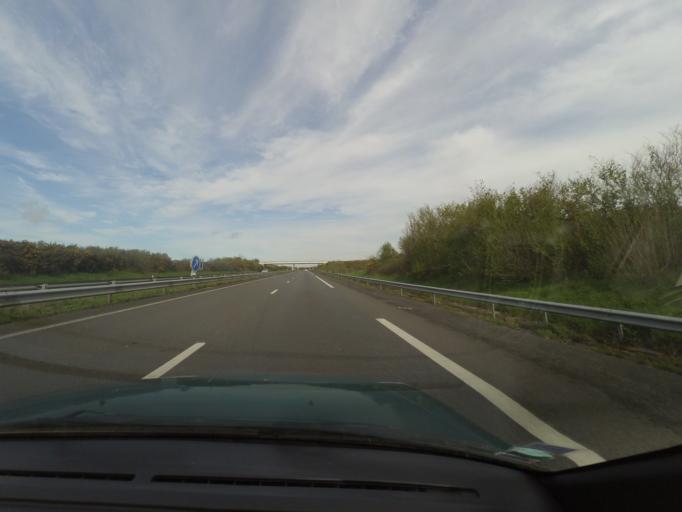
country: FR
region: Pays de la Loire
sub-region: Departement de la Loire-Atlantique
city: Le Bignon
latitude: 47.1026
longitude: -1.4768
